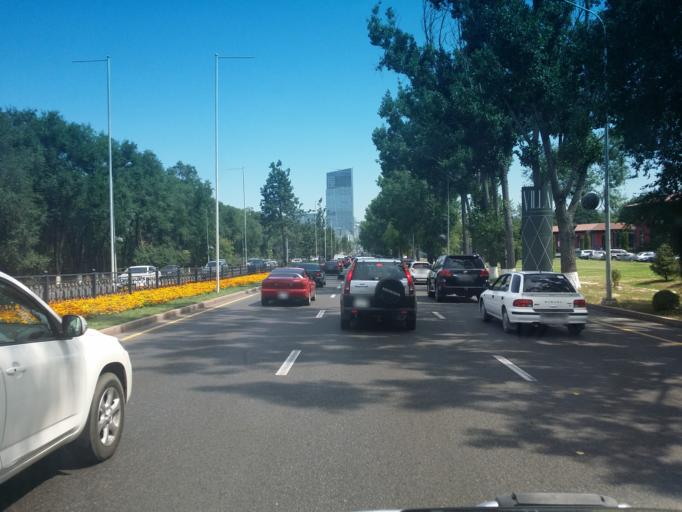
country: KZ
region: Almaty Qalasy
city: Almaty
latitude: 43.2109
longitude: 76.9183
